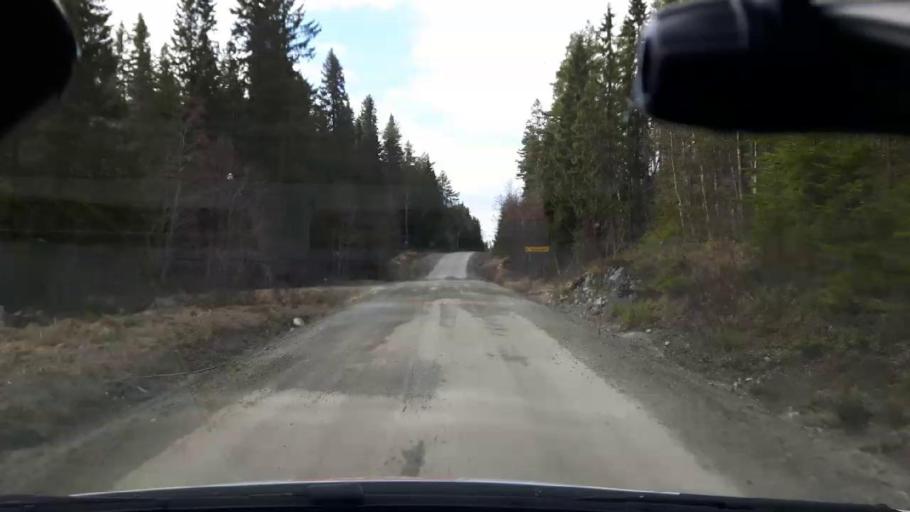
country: SE
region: Jaemtland
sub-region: Bergs Kommun
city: Hoverberg
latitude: 62.9027
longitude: 14.6409
